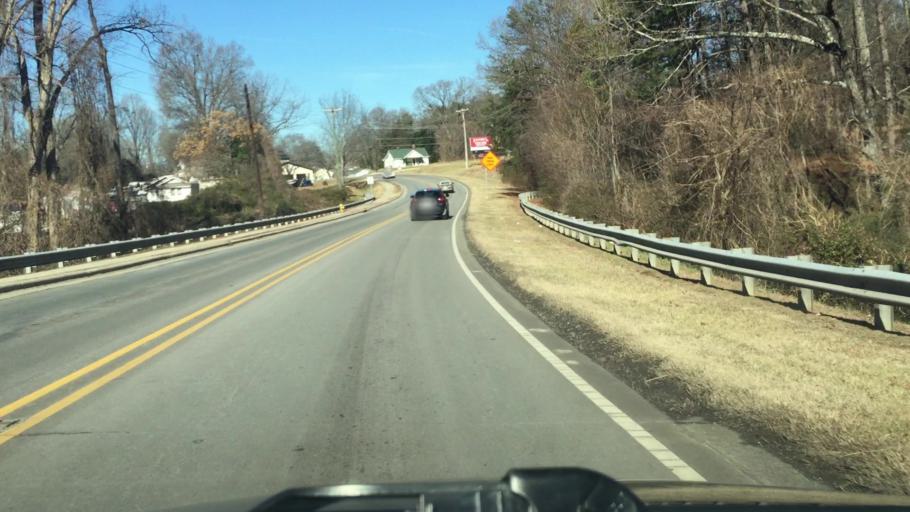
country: US
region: North Carolina
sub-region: Iredell County
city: Mooresville
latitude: 35.5875
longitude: -80.8127
